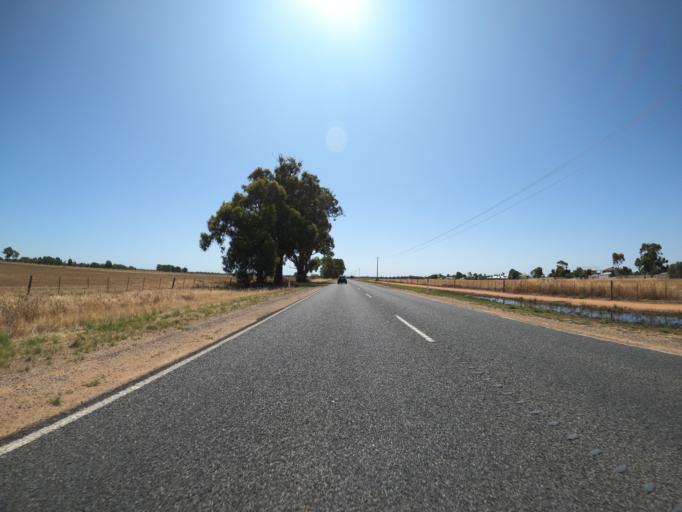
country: AU
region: Victoria
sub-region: Moira
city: Yarrawonga
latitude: -36.0241
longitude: 146.0642
